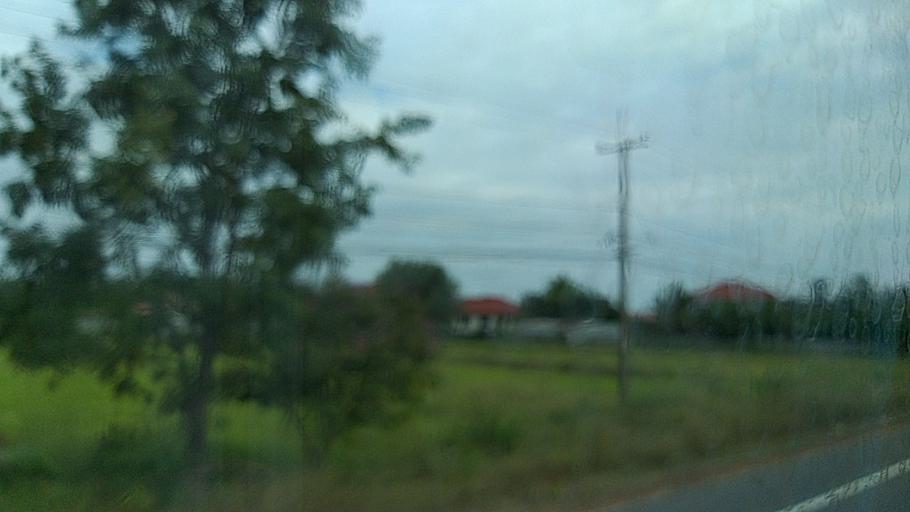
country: TH
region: Roi Et
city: Changhan
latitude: 16.1162
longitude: 103.4945
